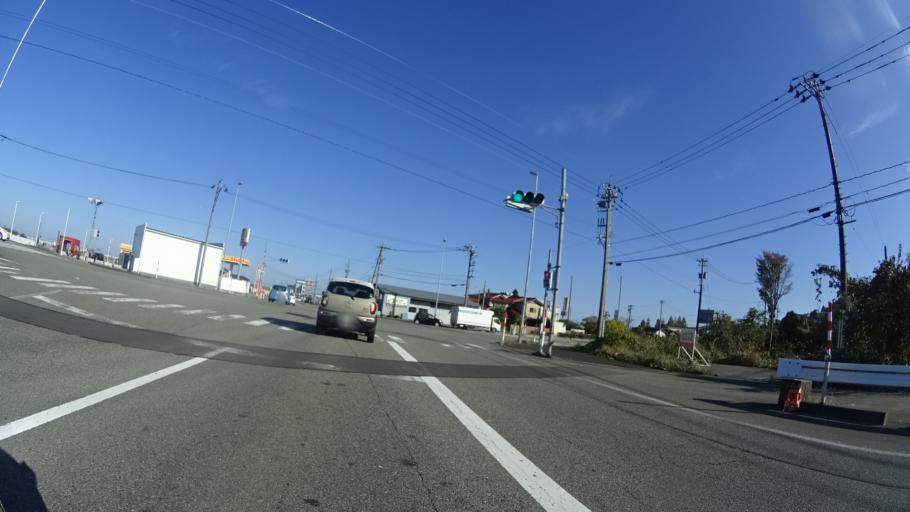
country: JP
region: Ishikawa
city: Komatsu
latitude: 36.3162
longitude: 136.3911
